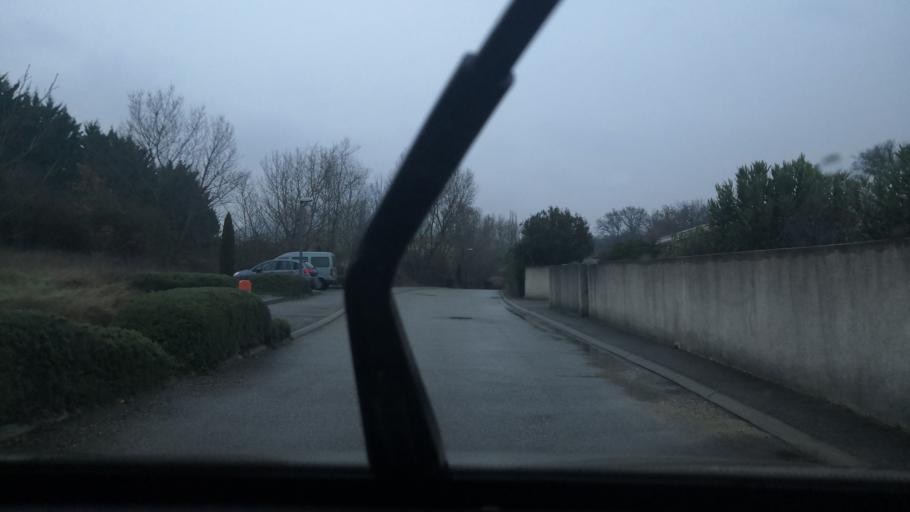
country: FR
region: Rhone-Alpes
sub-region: Departement de la Drome
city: Montboucher-sur-Jabron
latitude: 44.5416
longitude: 4.7988
